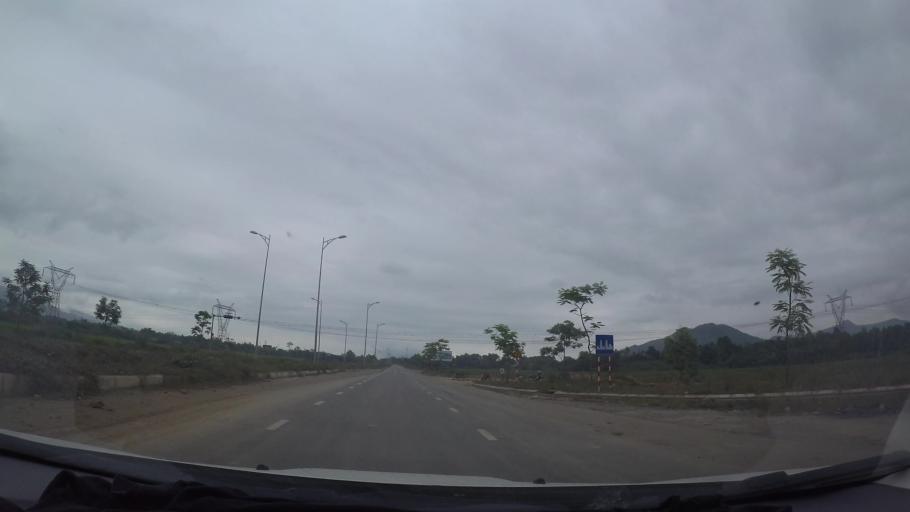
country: VN
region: Da Nang
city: Lien Chieu
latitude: 16.0748
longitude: 108.0887
